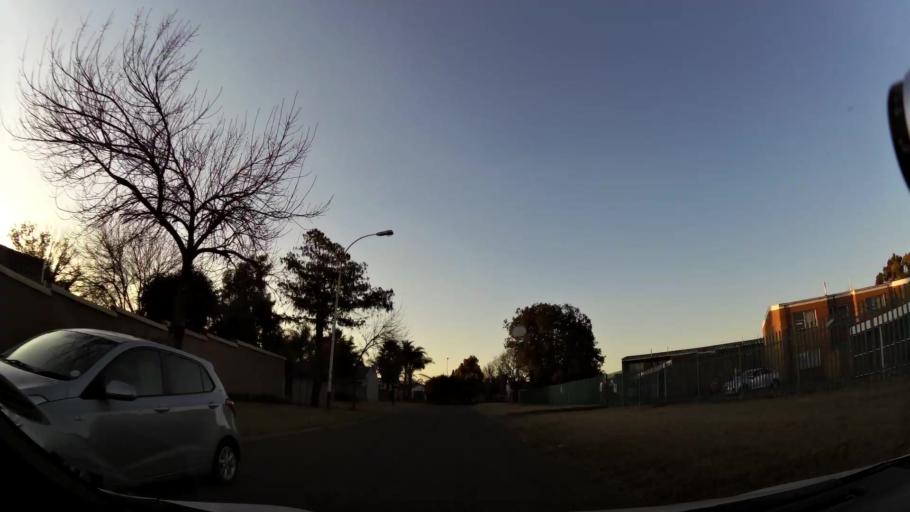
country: ZA
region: Gauteng
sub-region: Ekurhuleni Metropolitan Municipality
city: Germiston
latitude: -26.2675
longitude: 28.1520
